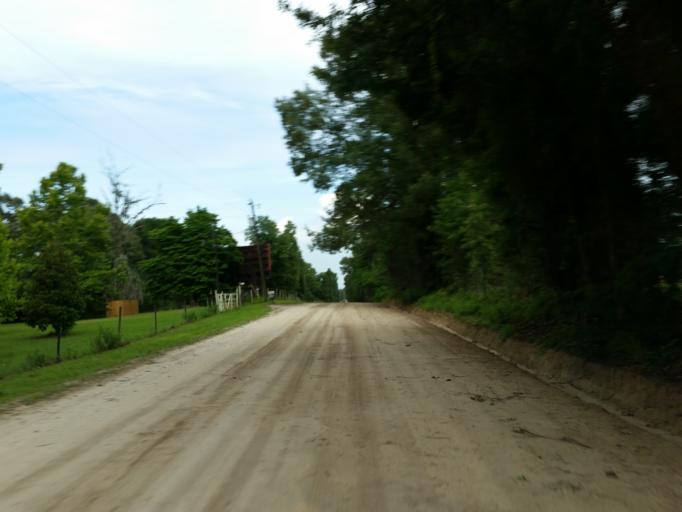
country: US
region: Florida
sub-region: Alachua County
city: High Springs
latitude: 29.9856
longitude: -82.5809
